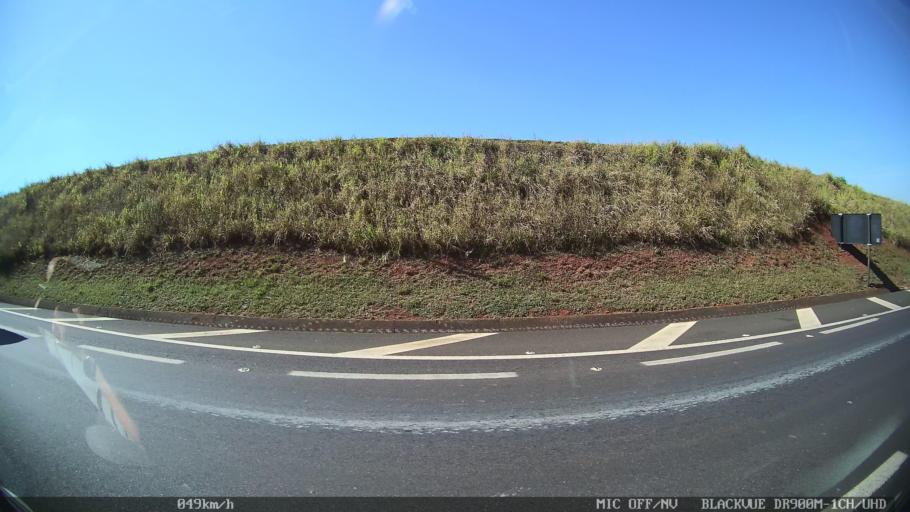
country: BR
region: Sao Paulo
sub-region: Franca
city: Franca
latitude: -20.6805
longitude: -47.4960
